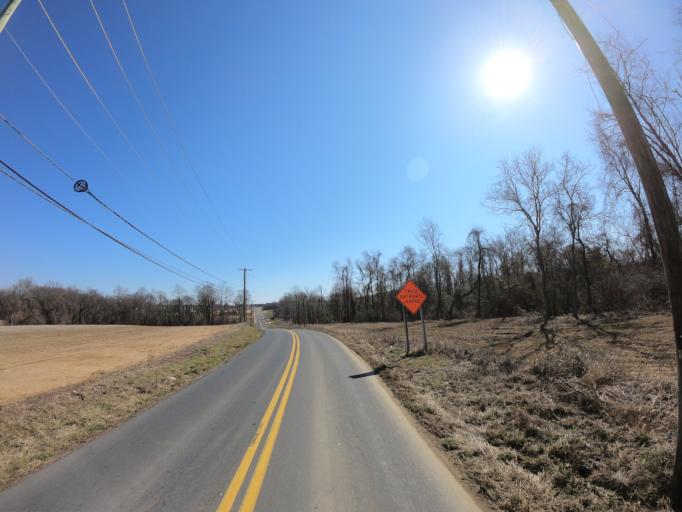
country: US
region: Delaware
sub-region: New Castle County
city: Middletown
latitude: 39.5325
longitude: -75.6915
